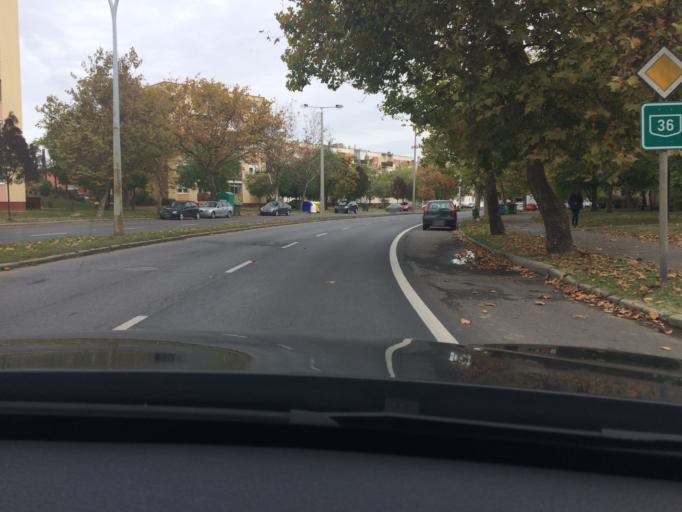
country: HU
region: Szabolcs-Szatmar-Bereg
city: Nyiregyhaza
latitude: 47.9646
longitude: 21.7068
